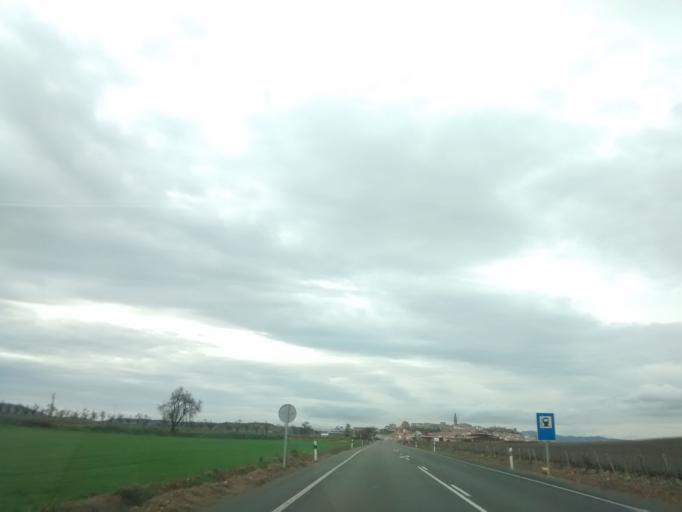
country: ES
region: La Rioja
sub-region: Provincia de La Rioja
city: Briones
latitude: 42.5330
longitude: -2.7663
